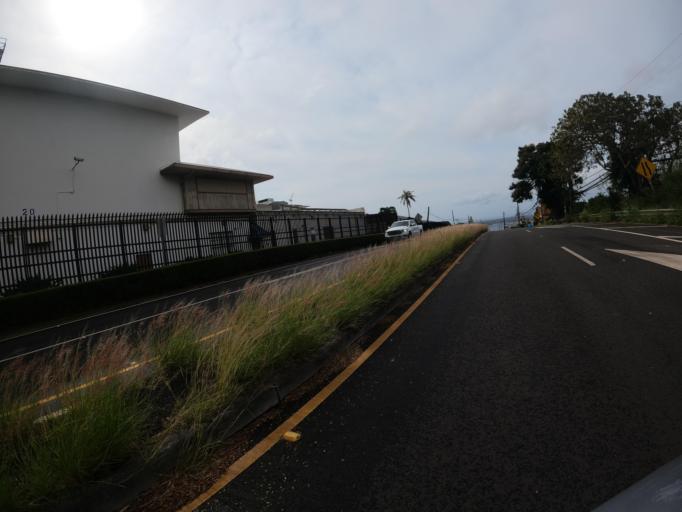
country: US
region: Hawaii
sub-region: Honolulu County
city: Halawa Heights
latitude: 21.3860
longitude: -157.9105
